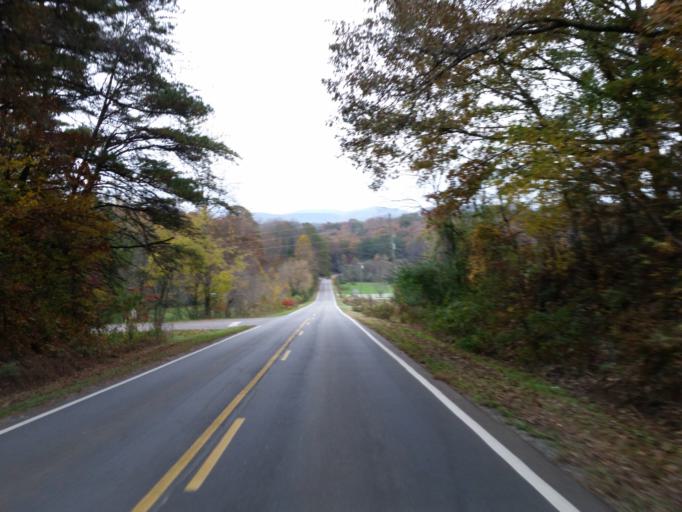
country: US
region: Georgia
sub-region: Gilmer County
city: Ellijay
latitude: 34.6448
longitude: -84.3407
